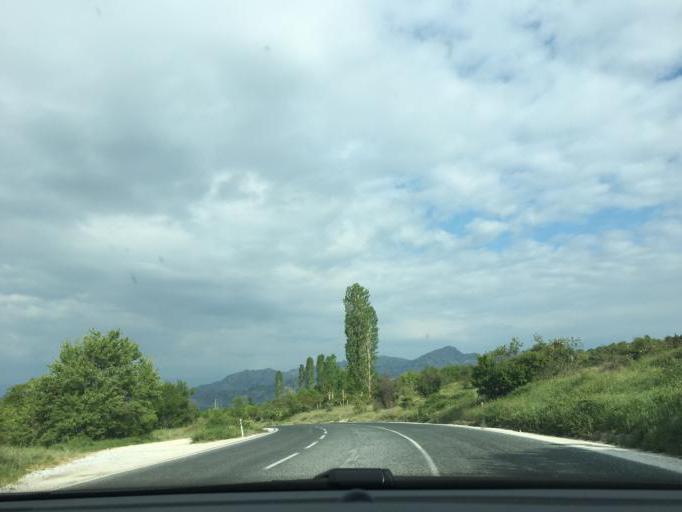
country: MK
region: Prilep
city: Prilep
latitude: 41.3684
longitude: 21.6412
